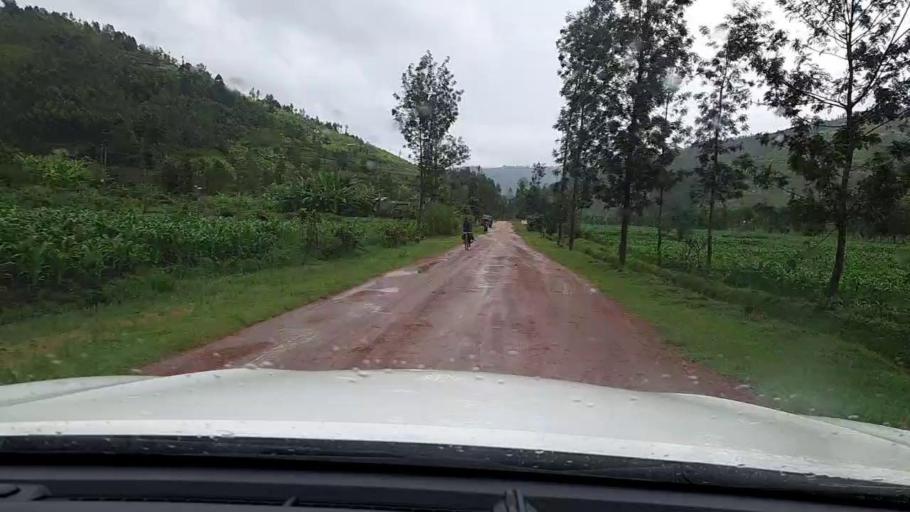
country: RW
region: Northern Province
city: Byumba
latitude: -1.7386
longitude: 29.9423
